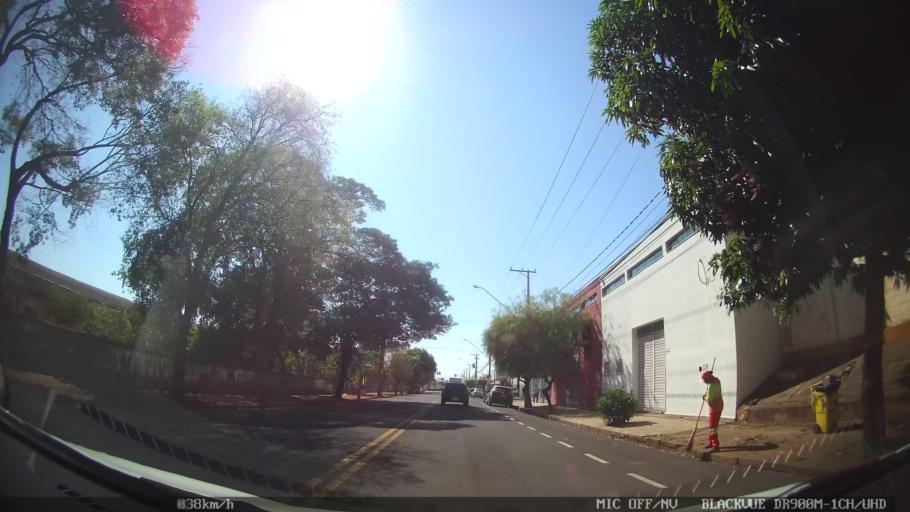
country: BR
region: Sao Paulo
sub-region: Sao Jose Do Rio Preto
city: Sao Jose do Rio Preto
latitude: -20.8019
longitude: -49.3978
